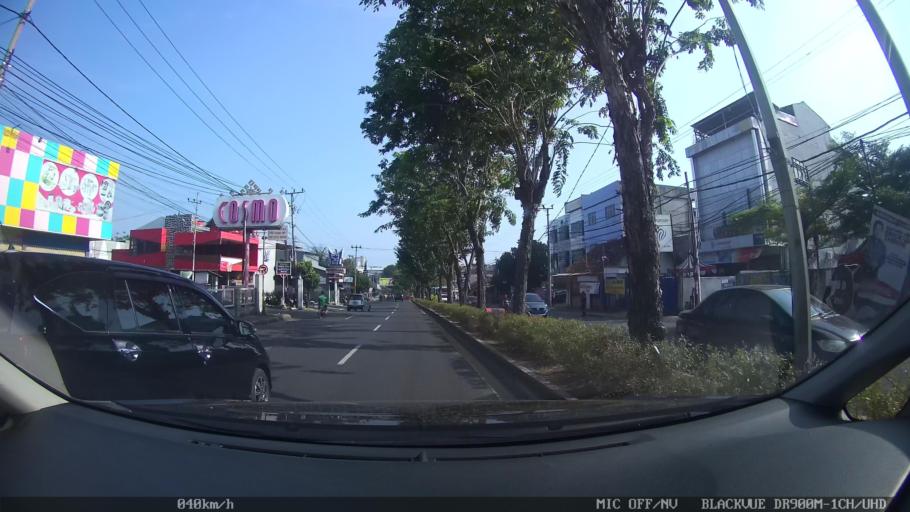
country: ID
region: Lampung
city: Kedaton
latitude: -5.3884
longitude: 105.2618
